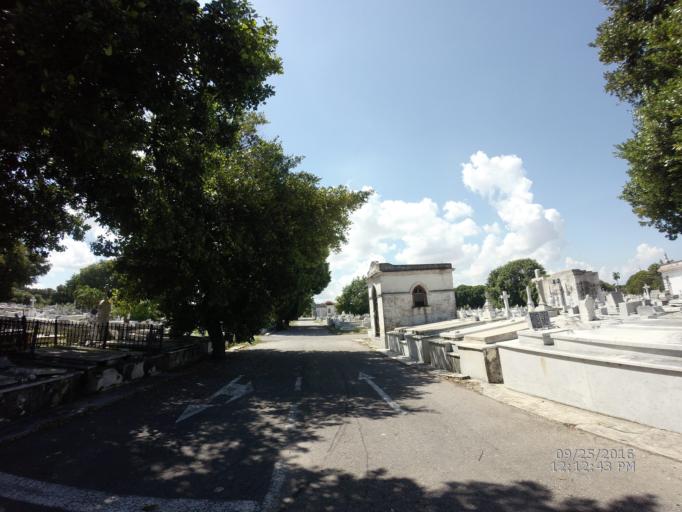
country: CU
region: La Habana
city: Havana
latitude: 23.1244
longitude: -82.3957
